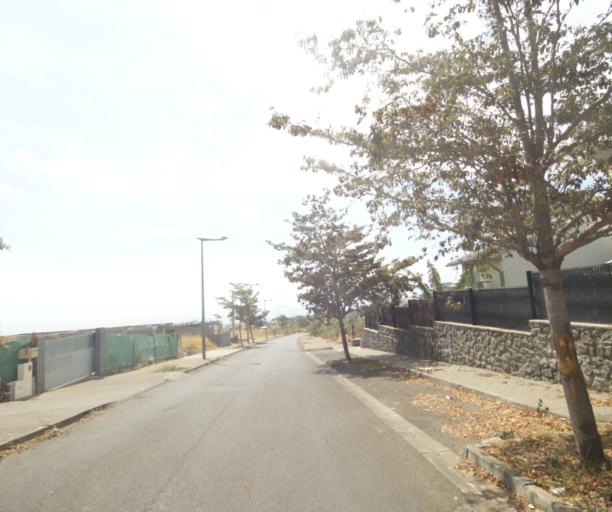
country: RE
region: Reunion
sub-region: Reunion
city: Saint-Paul
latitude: -21.0498
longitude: 55.2613
